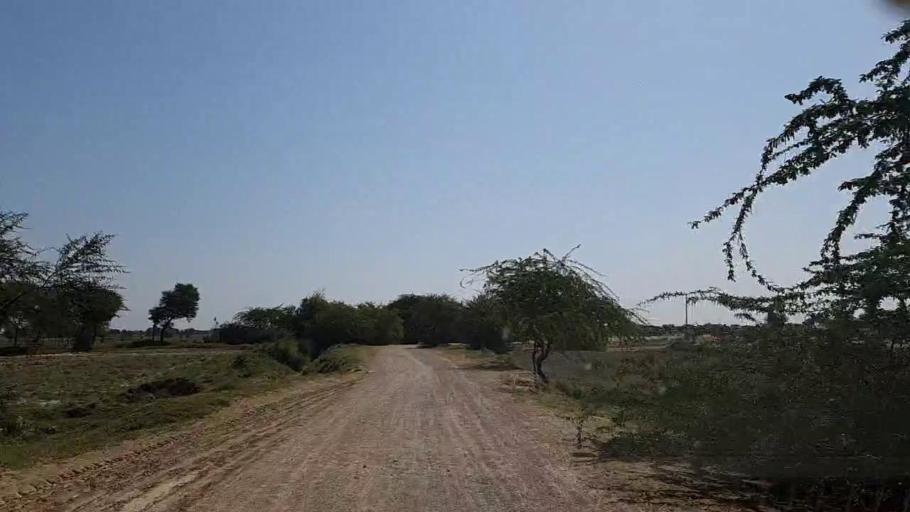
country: PK
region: Sindh
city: Mirpur Batoro
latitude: 24.6839
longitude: 68.2858
